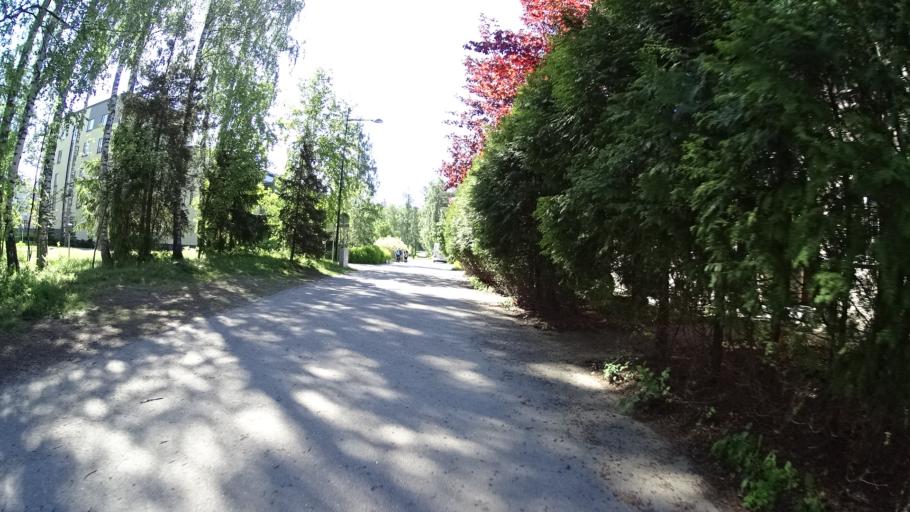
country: FI
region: Uusimaa
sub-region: Helsinki
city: Koukkuniemi
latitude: 60.1707
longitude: 24.7808
